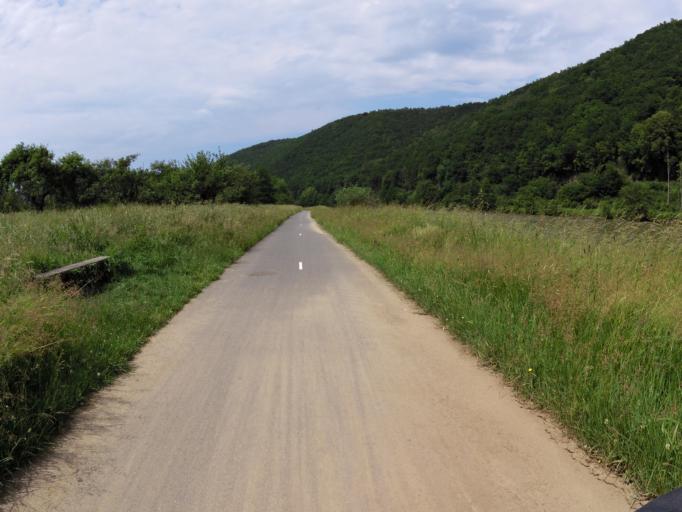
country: FR
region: Champagne-Ardenne
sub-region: Departement des Ardennes
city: Neufmanil
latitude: 49.8439
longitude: 4.7797
